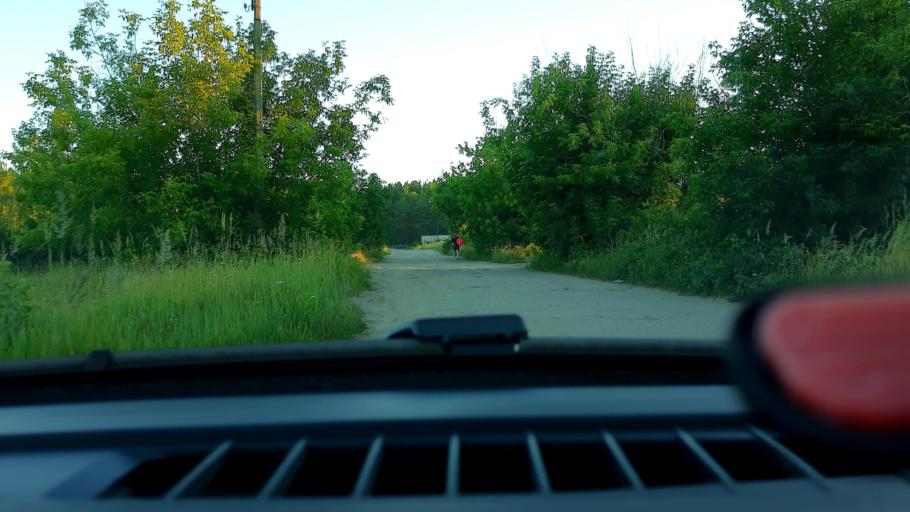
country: RU
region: Nizjnij Novgorod
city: Lukino
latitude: 56.3914
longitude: 43.7195
